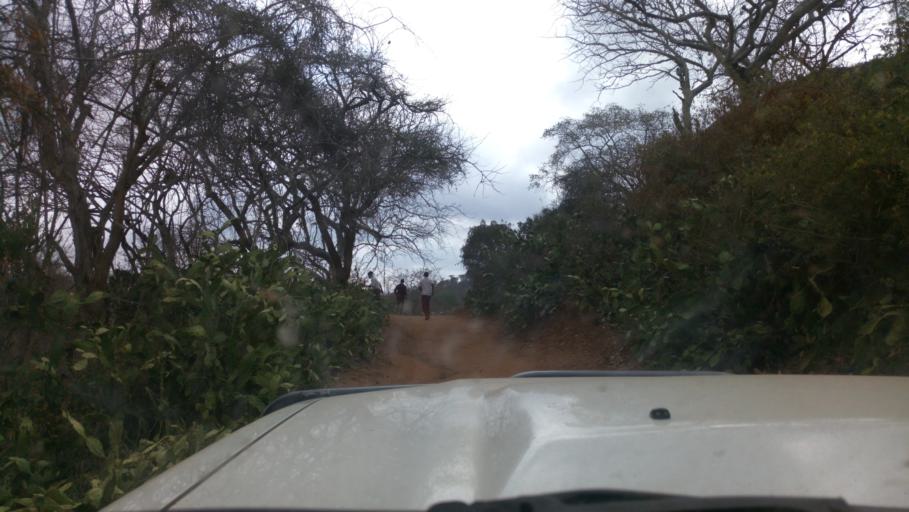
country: KE
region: Kitui
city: Kitui
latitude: -1.8548
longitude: 38.2508
